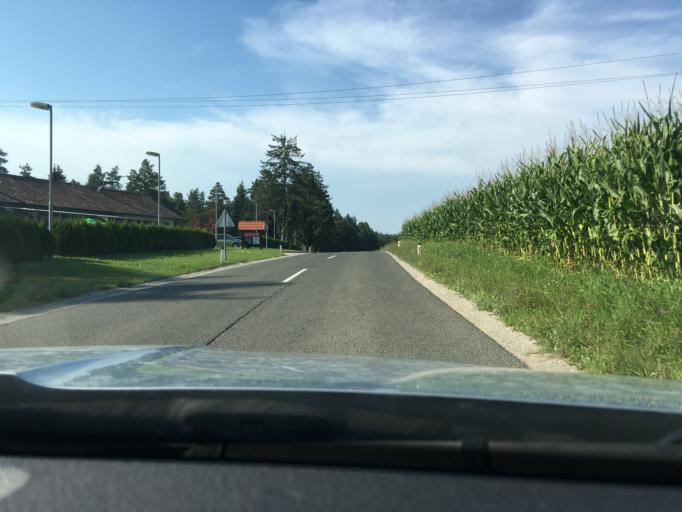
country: SI
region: Crnomelj
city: Crnomelj
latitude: 45.5464
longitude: 15.1613
